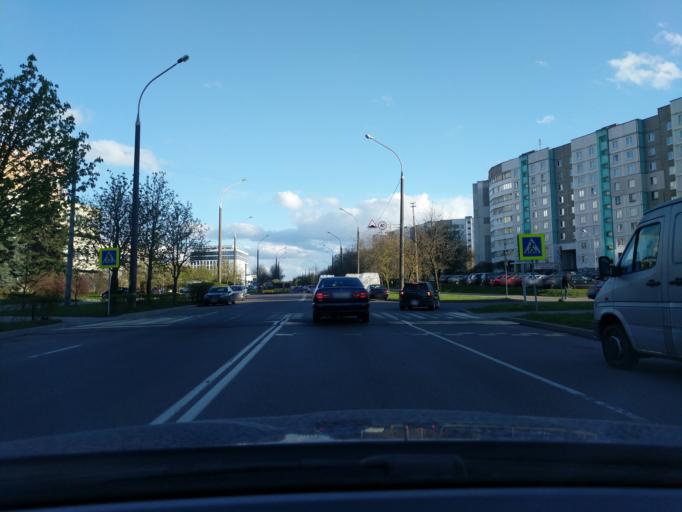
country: BY
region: Minsk
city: Novoye Medvezhino
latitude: 53.9128
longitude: 27.4505
